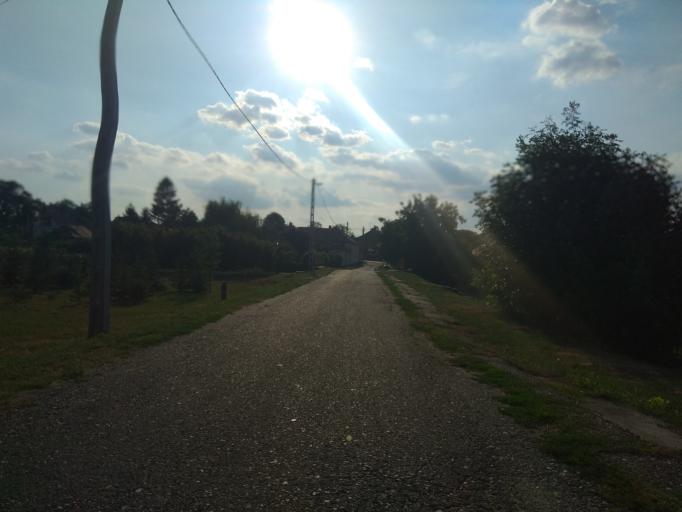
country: HU
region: Borsod-Abauj-Zemplen
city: Harsany
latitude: 47.9246
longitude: 20.7379
